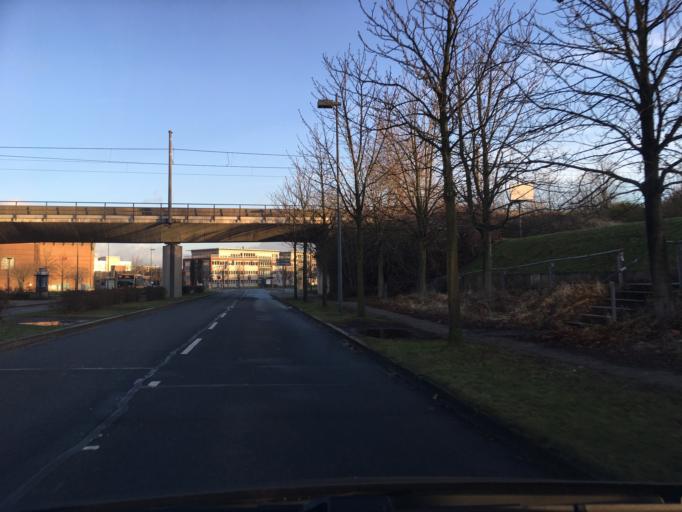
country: DE
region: North Rhine-Westphalia
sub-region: Regierungsbezirk Dusseldorf
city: Oberhausen
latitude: 51.4888
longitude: 6.8729
